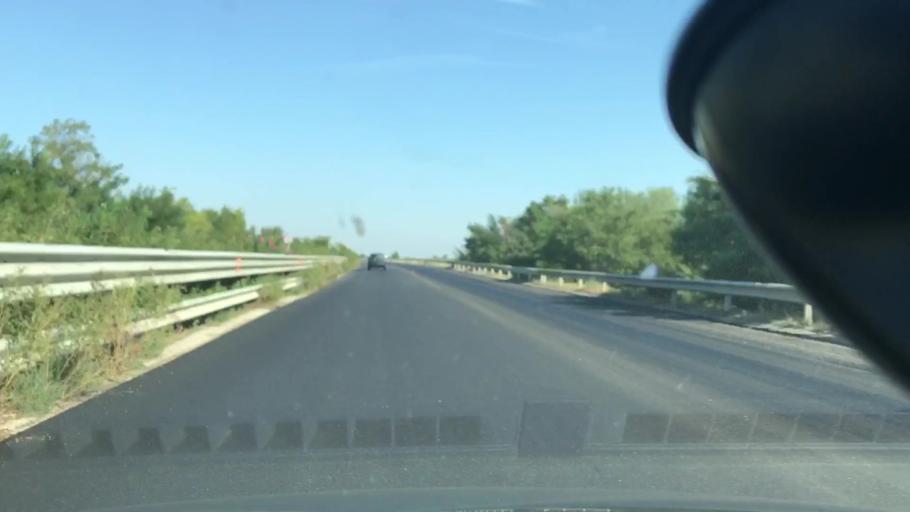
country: IT
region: Apulia
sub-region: Provincia di Foggia
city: Ascoli Satriano
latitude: 41.2748
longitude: 15.5534
